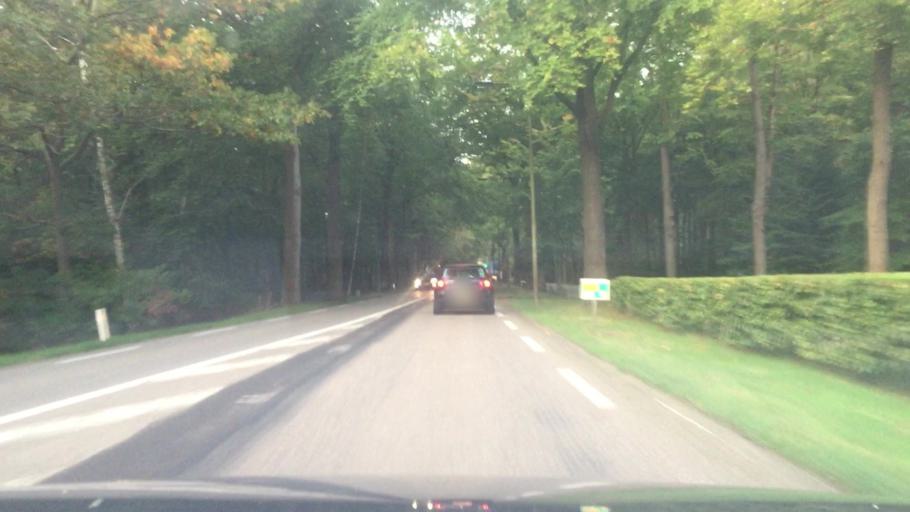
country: NL
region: Utrecht
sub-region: Gemeente De Bilt
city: De Bilt
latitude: 52.1541
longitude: 5.2269
